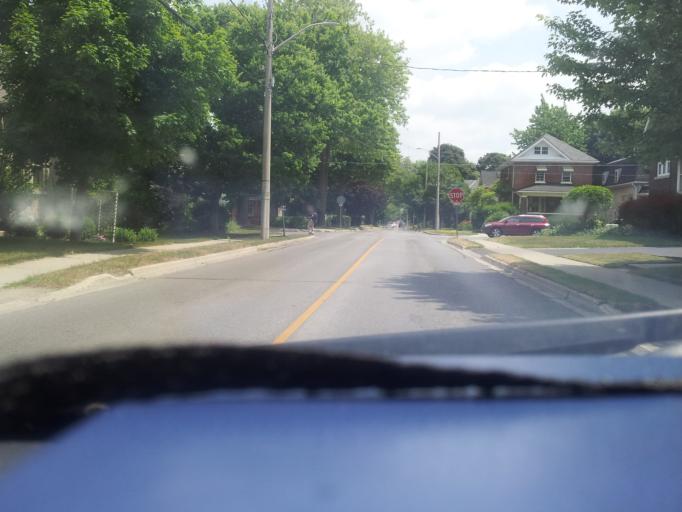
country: CA
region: Ontario
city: Stratford
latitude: 43.3673
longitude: -80.9740
